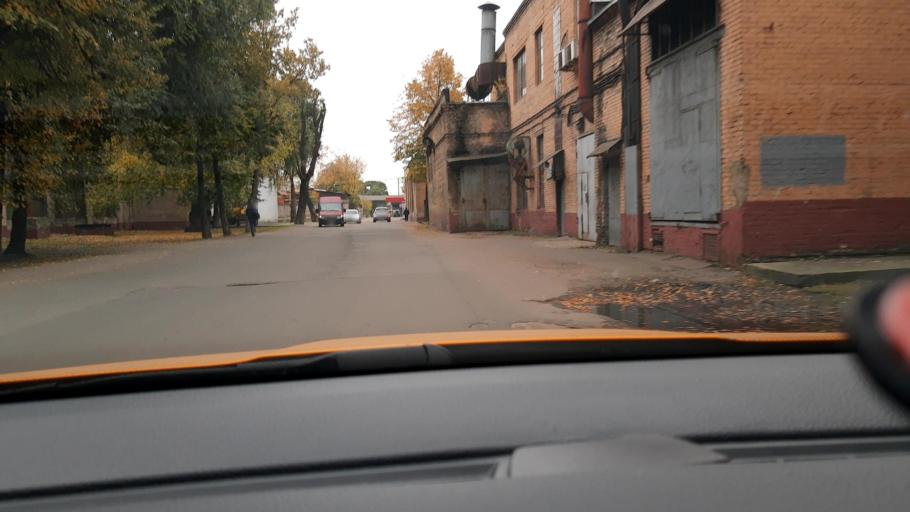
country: RU
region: Moscow
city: Taganskiy
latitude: 55.7188
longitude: 37.6851
